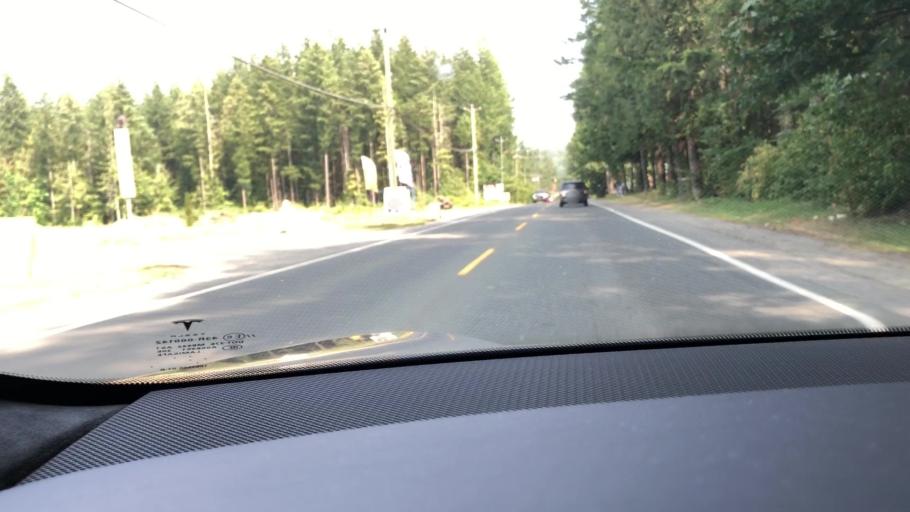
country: CA
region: British Columbia
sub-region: Fraser Valley Regional District
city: Chilliwack
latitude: 49.0749
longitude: -121.9698
